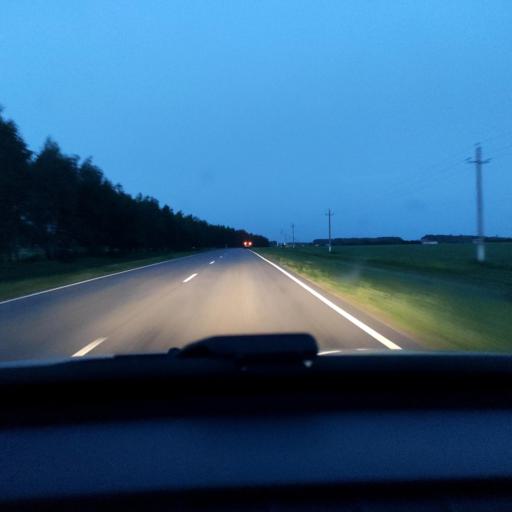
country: RU
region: Voronezj
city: Panino
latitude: 51.6553
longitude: 40.0023
